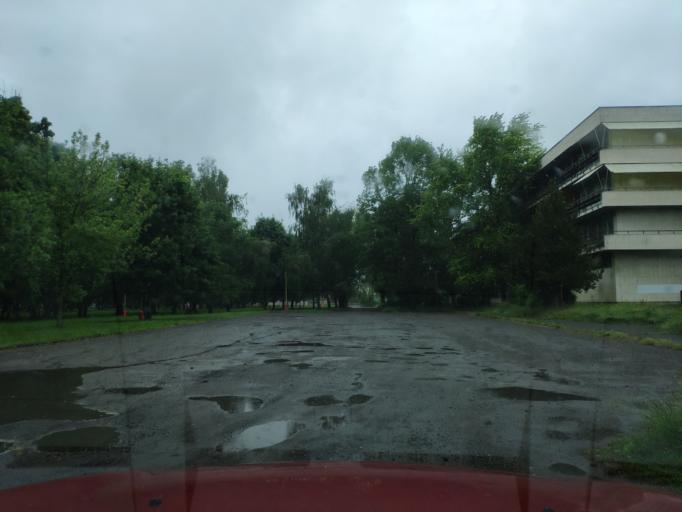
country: SK
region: Kosicky
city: Cierna nad Tisou
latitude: 48.4183
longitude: 22.0905
